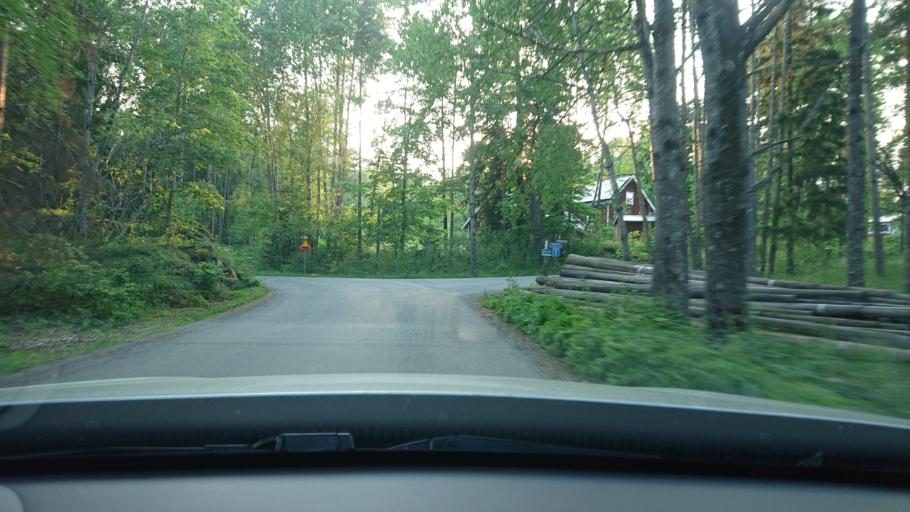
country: SE
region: Stockholm
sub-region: Osterakers Kommun
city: Akersberga
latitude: 59.5026
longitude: 18.3467
